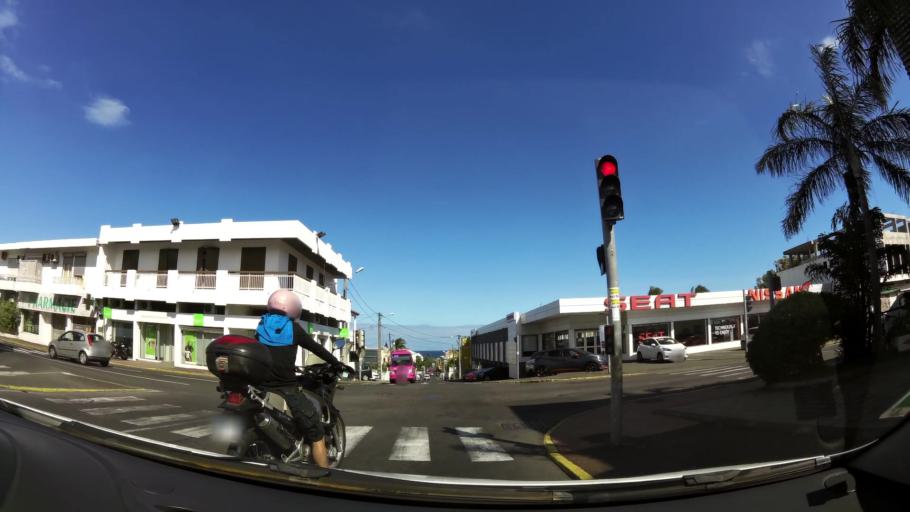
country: RE
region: Reunion
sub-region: Reunion
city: Saint-Pierre
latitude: -21.3363
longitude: 55.4704
